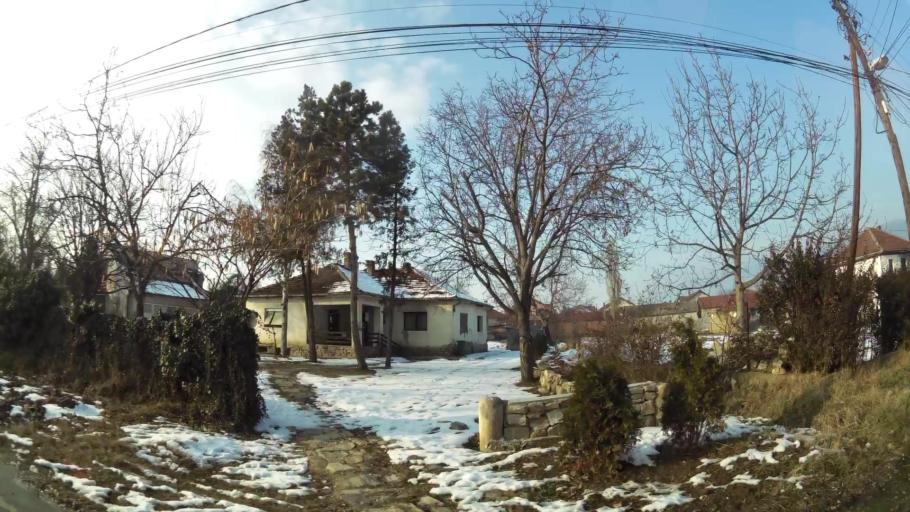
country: MK
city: Creshevo
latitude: 42.0260
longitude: 21.5121
